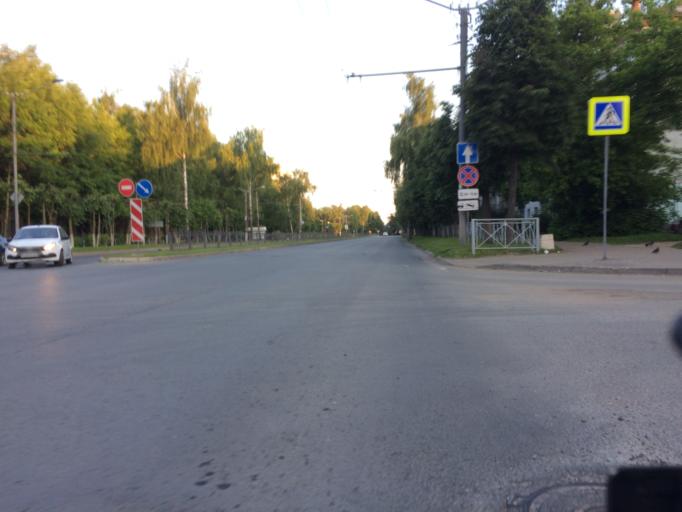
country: RU
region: Mariy-El
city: Yoshkar-Ola
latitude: 56.6439
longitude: 47.8799
